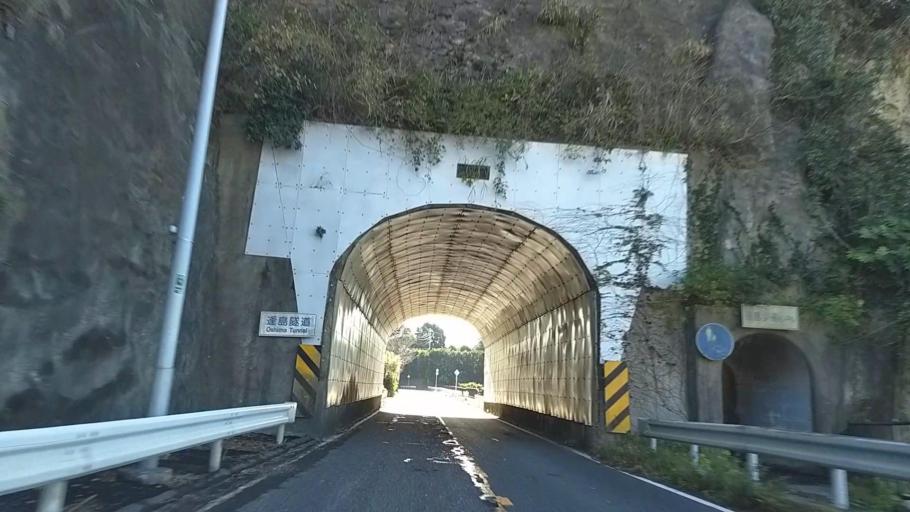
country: JP
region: Chiba
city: Tateyama
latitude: 35.0509
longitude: 139.8331
